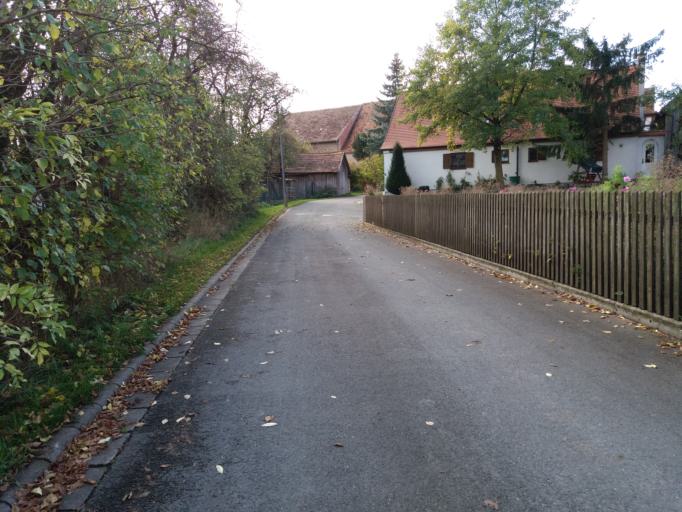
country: DE
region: Bavaria
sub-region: Regierungsbezirk Mittelfranken
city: Illesheim
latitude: 49.4602
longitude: 10.4120
